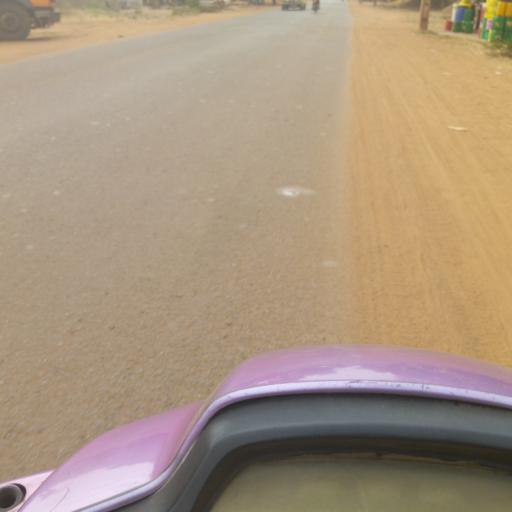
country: ML
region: Bamako
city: Bamako
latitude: 12.6604
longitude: -7.9361
